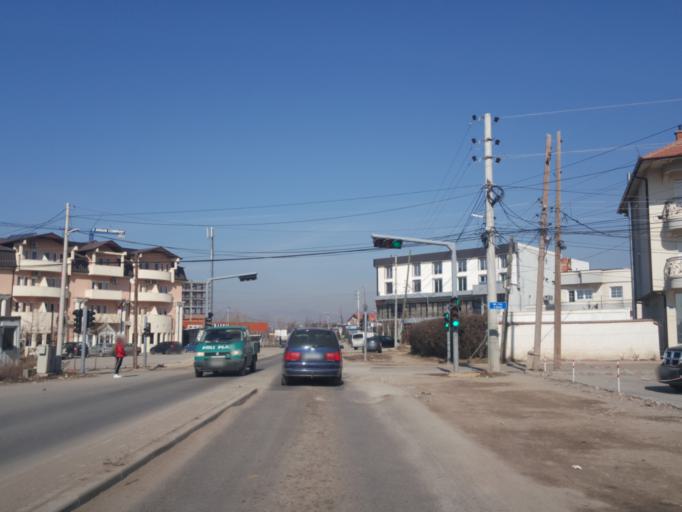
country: XK
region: Mitrovica
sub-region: Vushtrri
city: Vushtrri
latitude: 42.8173
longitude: 20.9822
